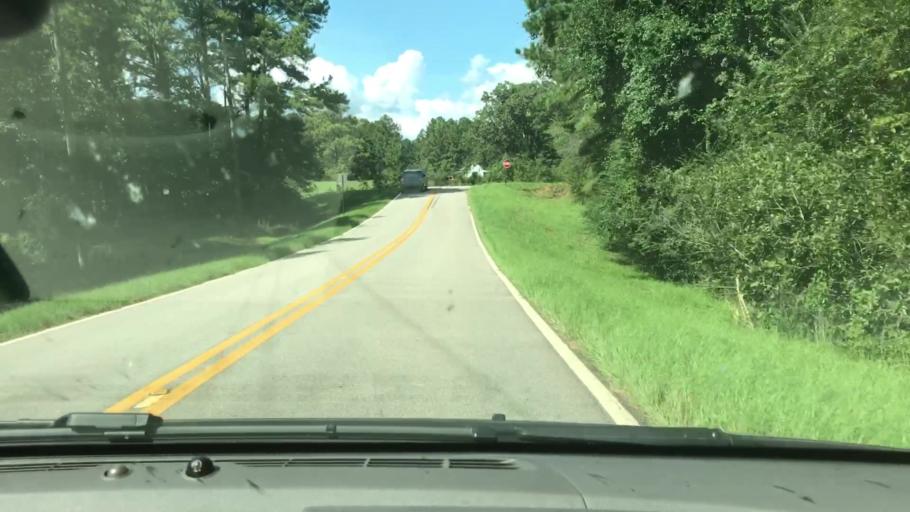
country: US
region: Georgia
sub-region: Heard County
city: Franklin
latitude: 33.1447
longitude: -85.1153
